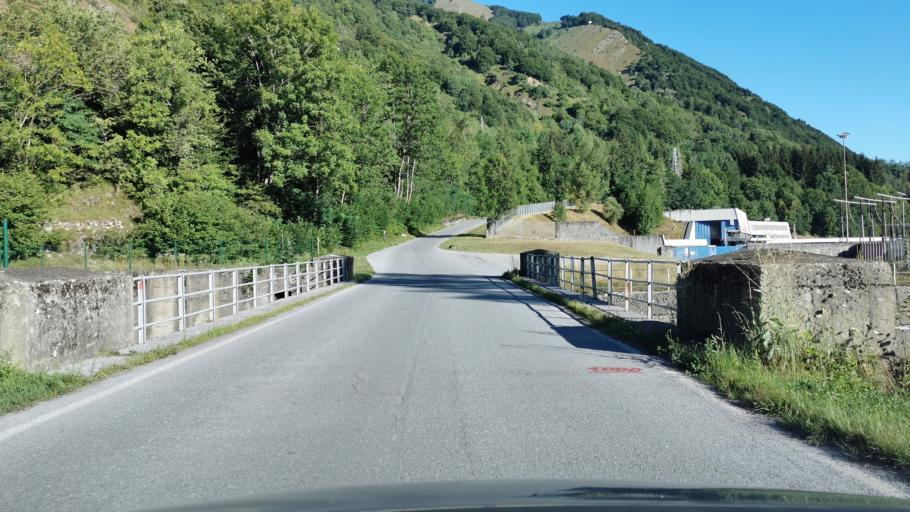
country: IT
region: Piedmont
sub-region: Provincia di Cuneo
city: Entracque
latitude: 44.2262
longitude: 7.3914
